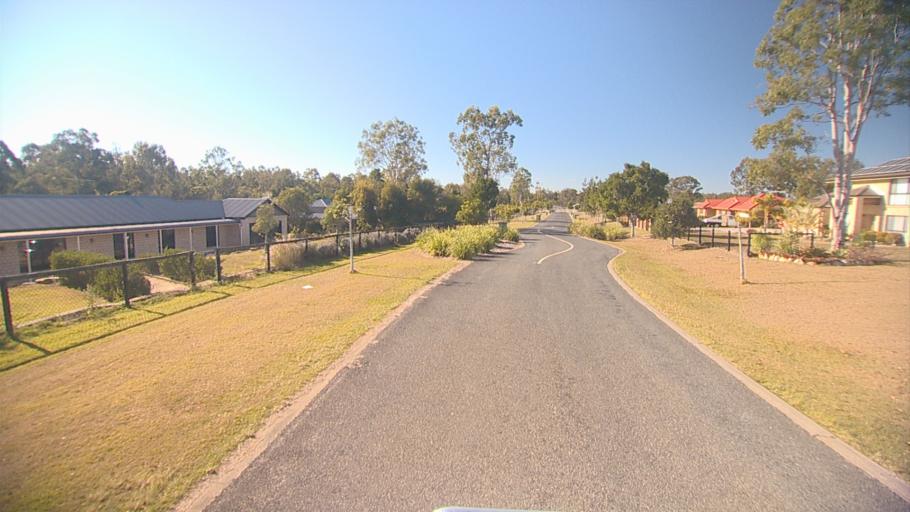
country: AU
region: Queensland
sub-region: Logan
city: North Maclean
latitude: -27.7481
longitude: 152.9643
